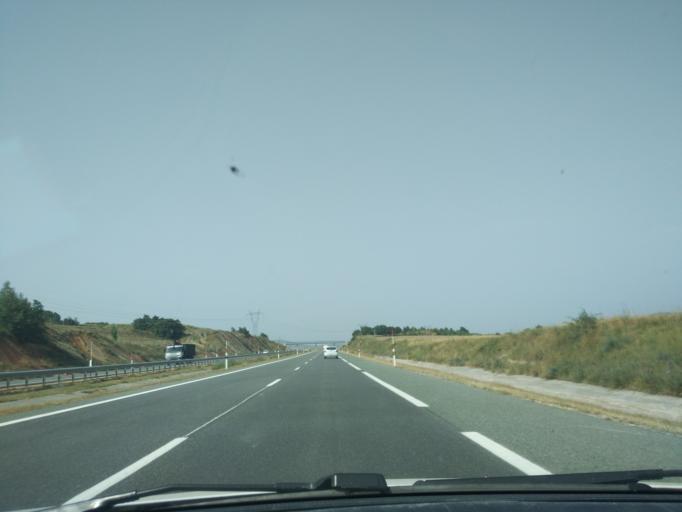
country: ES
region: Cantabria
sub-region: Provincia de Cantabria
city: Mataporquera
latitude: 42.8275
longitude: -4.2022
